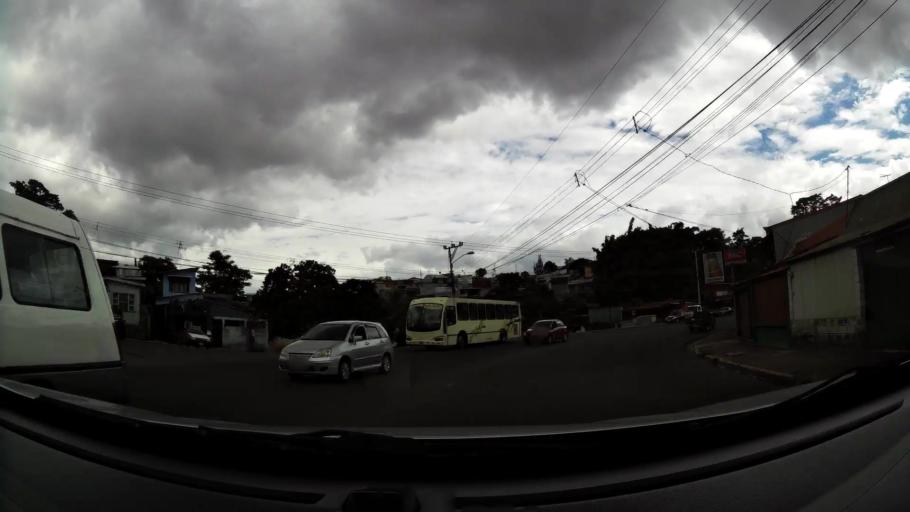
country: CR
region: San Jose
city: Alajuelita
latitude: 9.9016
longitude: -84.0897
